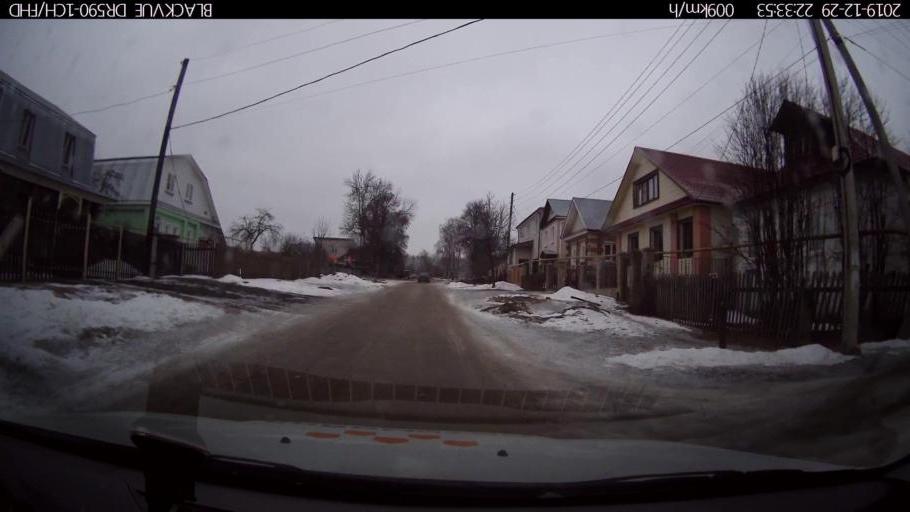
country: RU
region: Nizjnij Novgorod
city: Afonino
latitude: 56.2032
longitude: 43.9860
